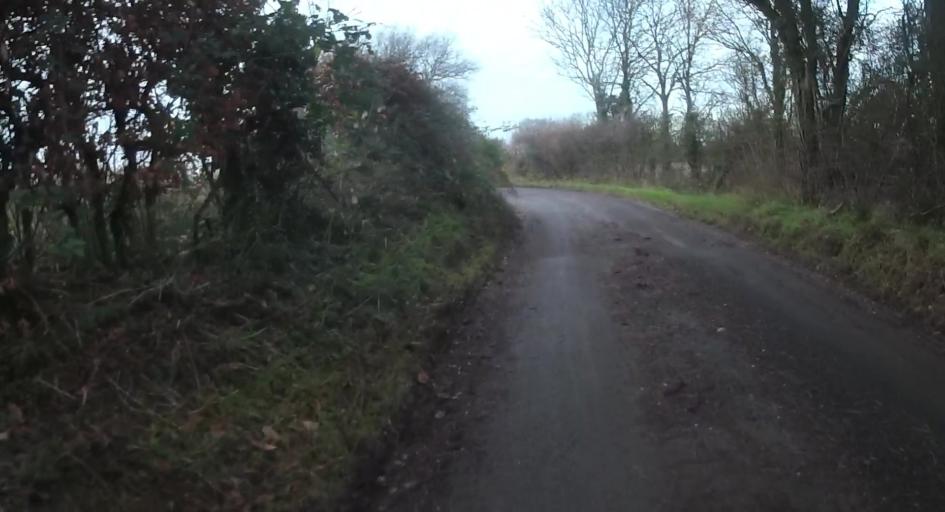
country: GB
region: England
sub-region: Hampshire
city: Kingsclere
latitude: 51.2880
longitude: -1.1804
